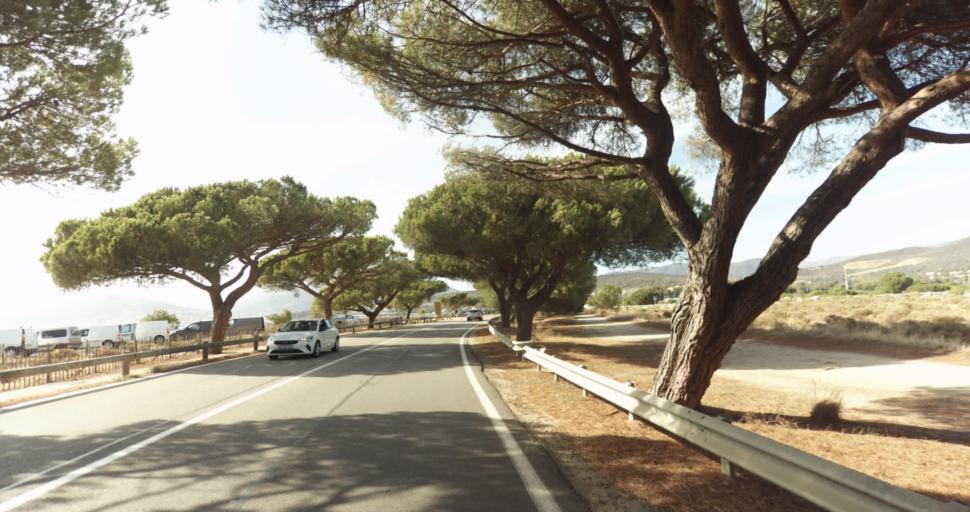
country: FR
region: Corsica
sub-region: Departement de la Corse-du-Sud
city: Ajaccio
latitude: 41.9200
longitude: 8.7888
